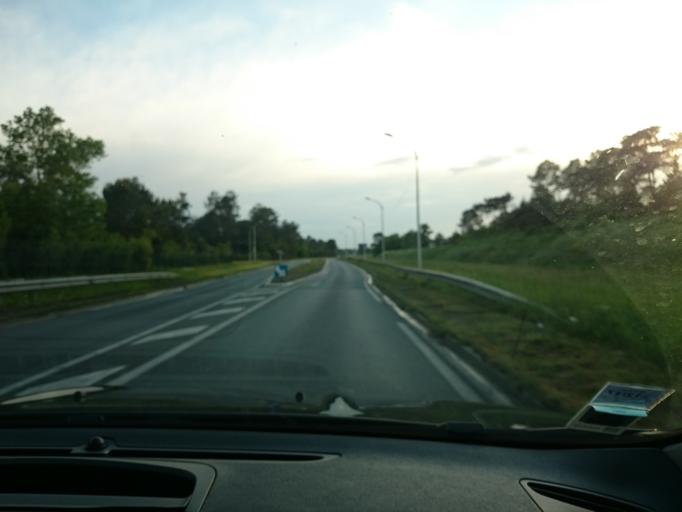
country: FR
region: Aquitaine
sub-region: Departement de la Gironde
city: Pessac
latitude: 44.8149
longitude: -0.6849
